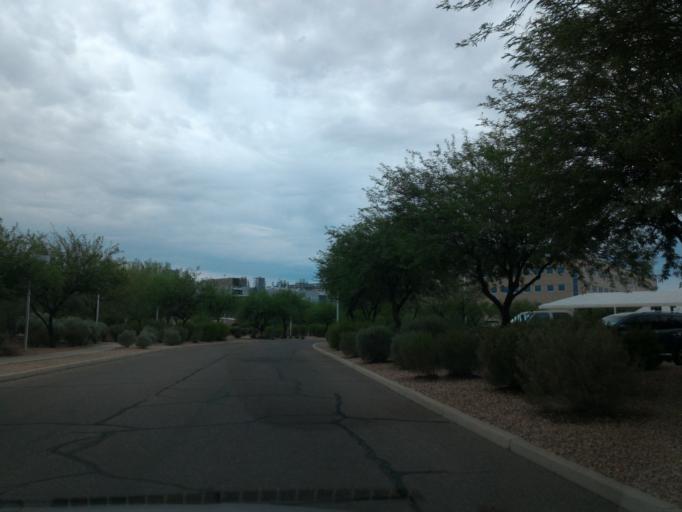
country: US
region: Arizona
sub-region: Maricopa County
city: Sun Lakes
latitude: 33.2431
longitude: -111.8827
